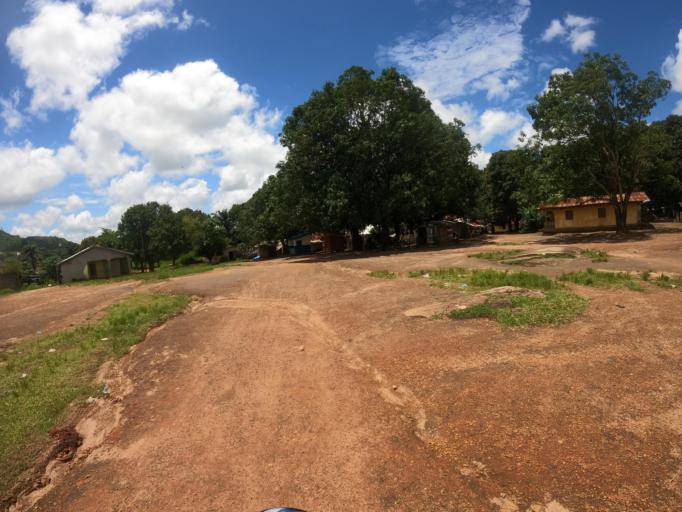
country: SL
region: Northern Province
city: Makeni
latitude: 8.8914
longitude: -12.0698
